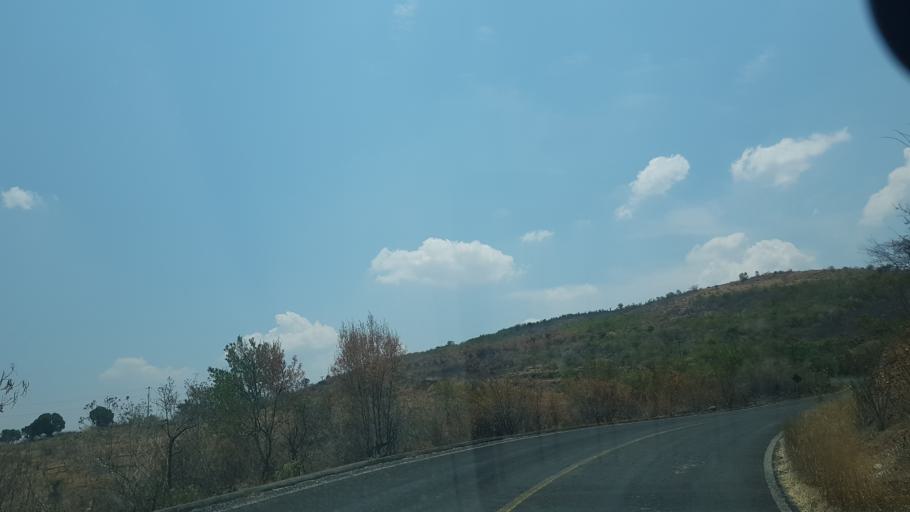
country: MX
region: Puebla
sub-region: Atzitzihuacan
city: Santiago Atzitzihuacan
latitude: 18.8364
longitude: -98.5871
